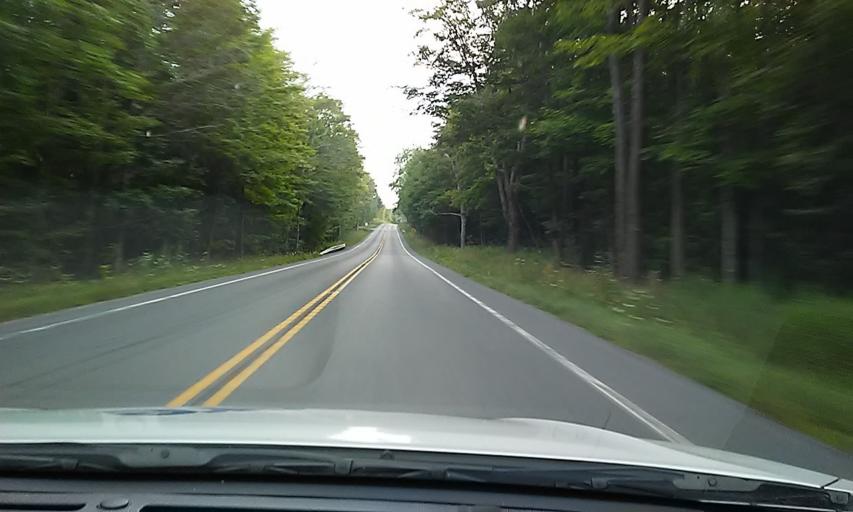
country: US
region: Pennsylvania
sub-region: McKean County
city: Kane
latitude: 41.5873
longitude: -78.8457
